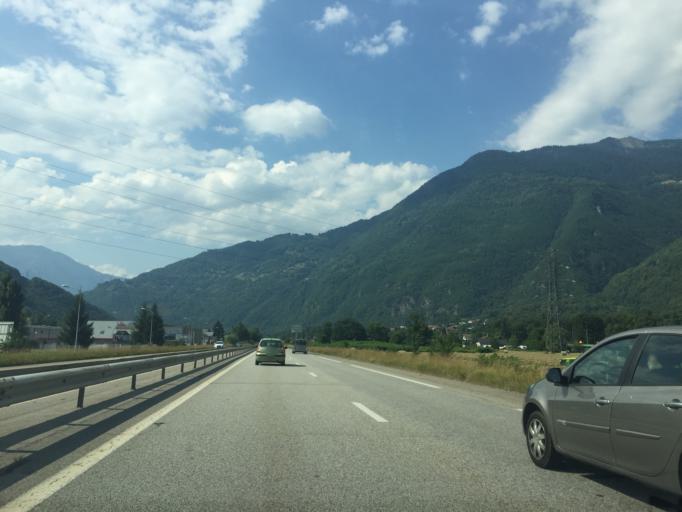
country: FR
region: Rhone-Alpes
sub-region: Departement de la Savoie
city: La Bathie
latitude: 45.6400
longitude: 6.4404
